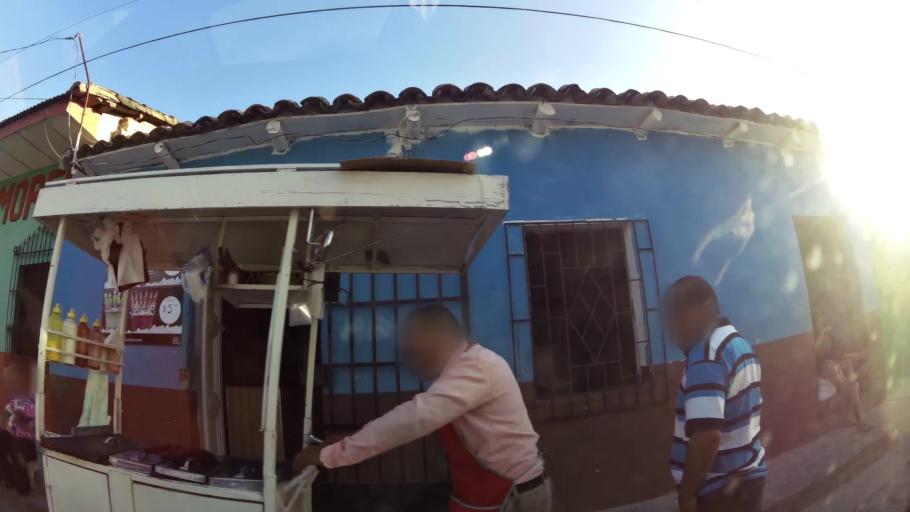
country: SV
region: Santa Ana
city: Metapan
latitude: 14.3302
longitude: -89.4481
